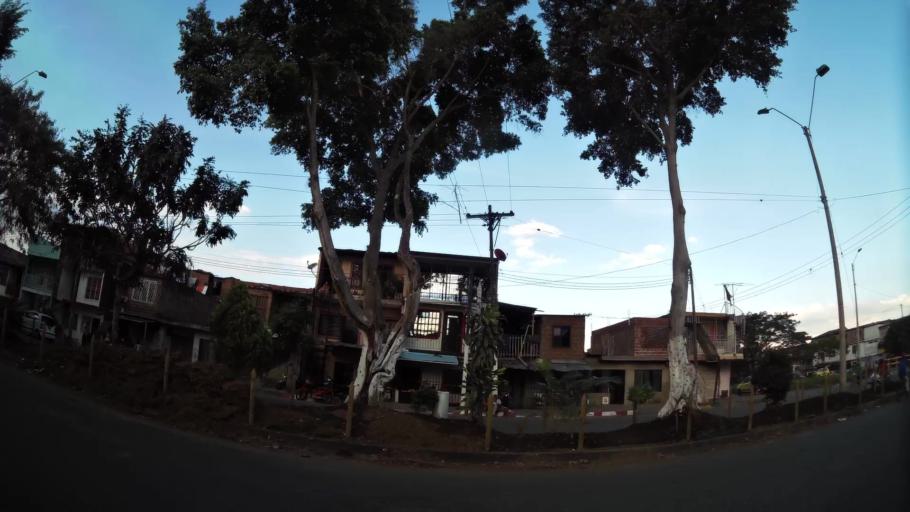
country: CO
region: Valle del Cauca
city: Cali
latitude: 3.4118
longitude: -76.5008
